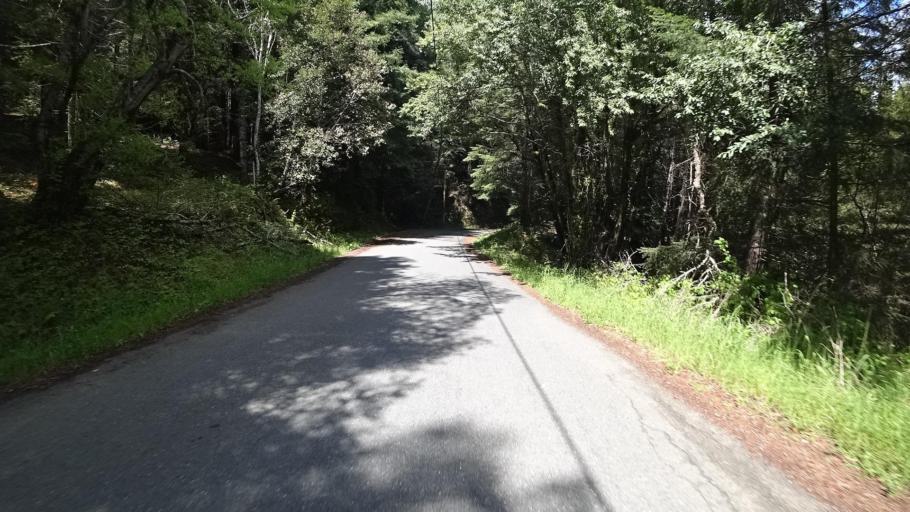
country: US
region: California
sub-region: Humboldt County
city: Blue Lake
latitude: 40.8438
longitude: -123.8985
